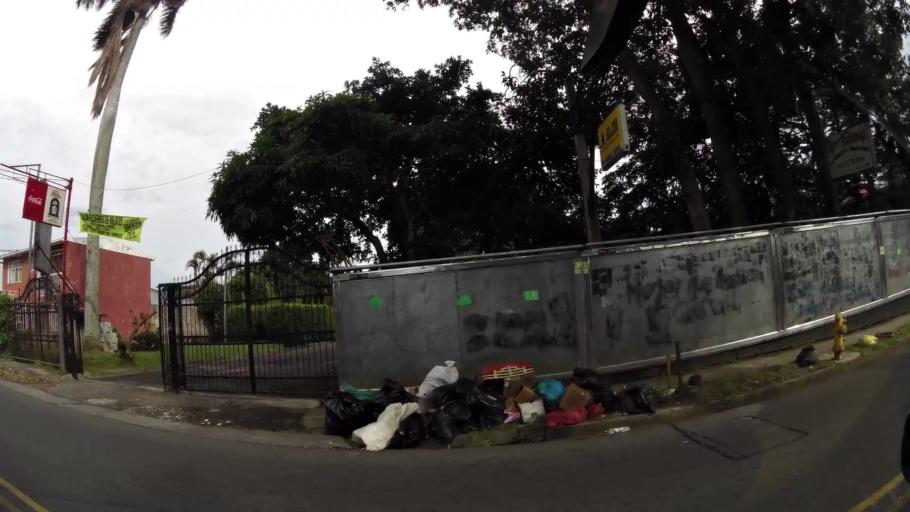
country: CR
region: San Jose
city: Calle Blancos
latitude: 9.9619
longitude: -84.0631
